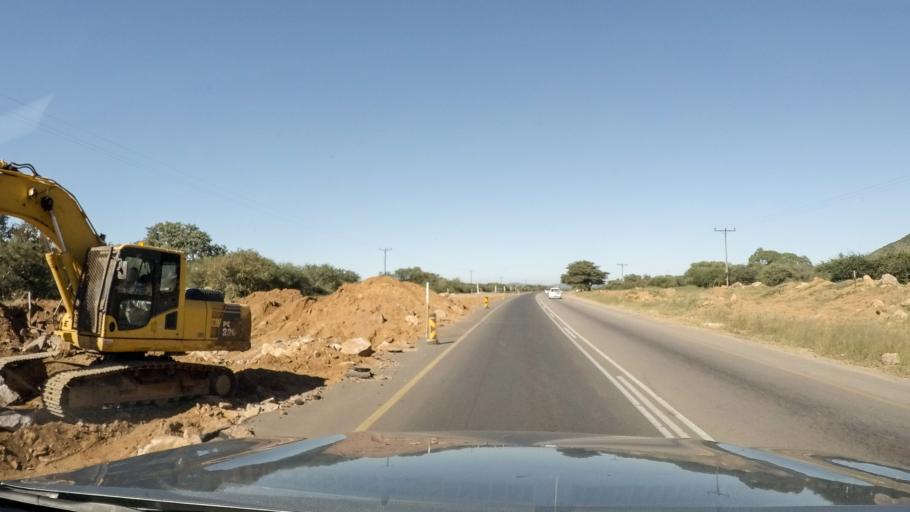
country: BW
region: South East
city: Gaborone
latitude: -24.7105
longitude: 25.8663
